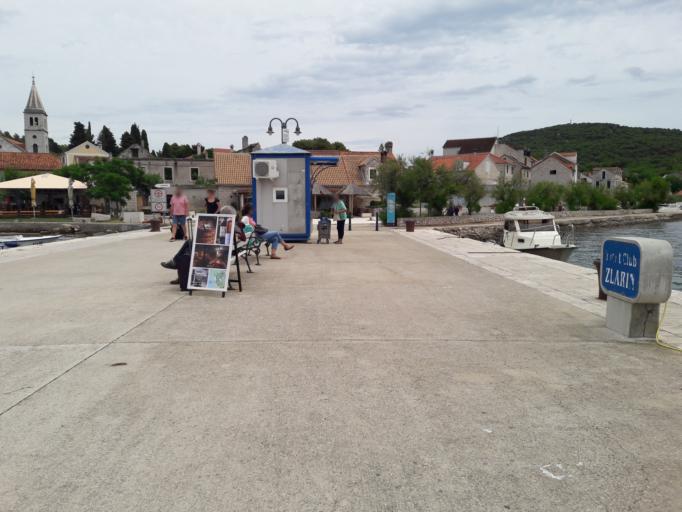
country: HR
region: Sibensko-Kniniska
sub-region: Grad Sibenik
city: Sibenik
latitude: 43.6992
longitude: 15.8341
